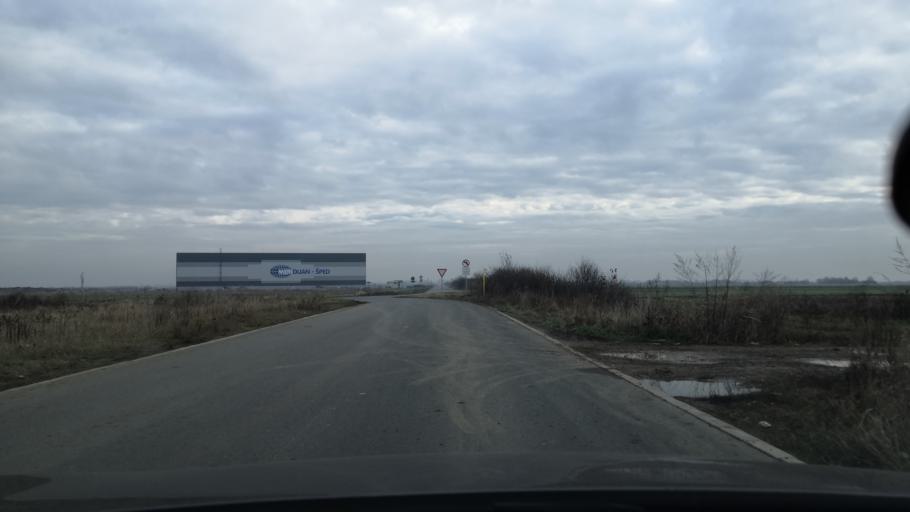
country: RS
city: Ugrinovci
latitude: 44.8823
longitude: 20.1489
